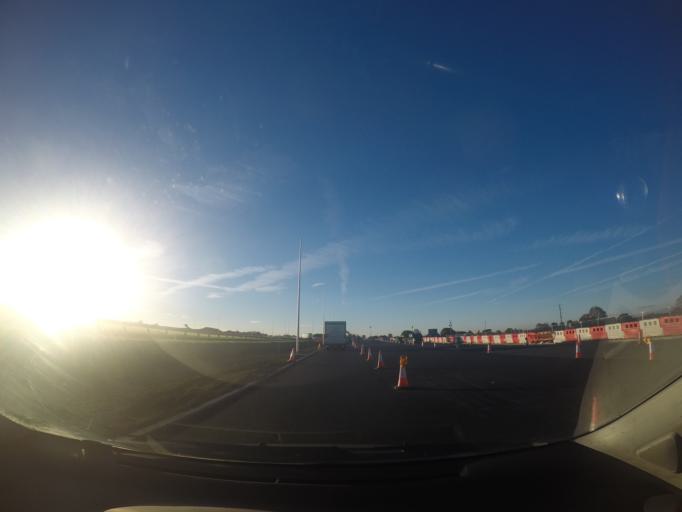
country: GB
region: England
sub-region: City of York
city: Nether Poppleton
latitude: 53.9576
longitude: -1.1499
